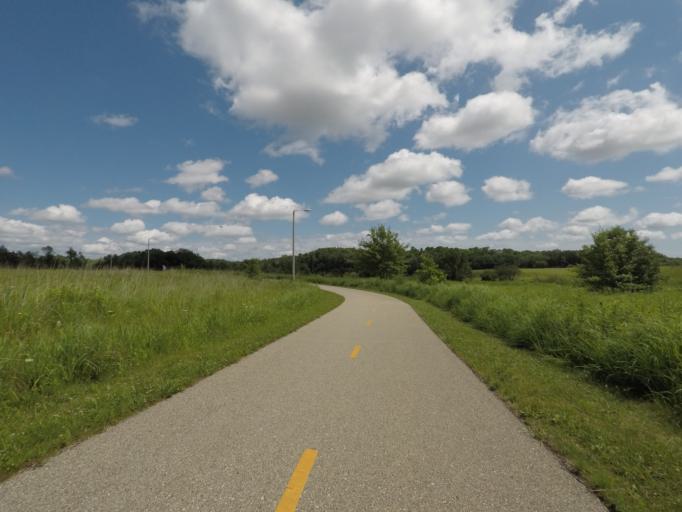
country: US
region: Wisconsin
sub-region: Dane County
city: Verona
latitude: 43.0238
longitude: -89.5316
